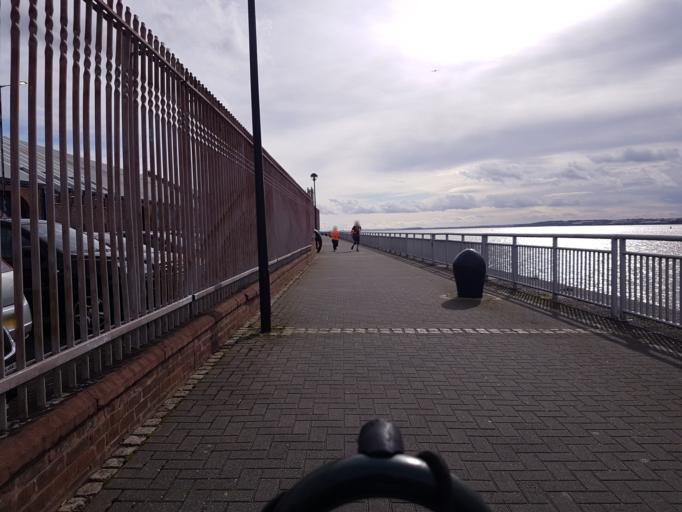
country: GB
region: England
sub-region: Metropolitan Borough of Wirral
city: New Ferry
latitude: 53.3834
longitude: -2.9811
